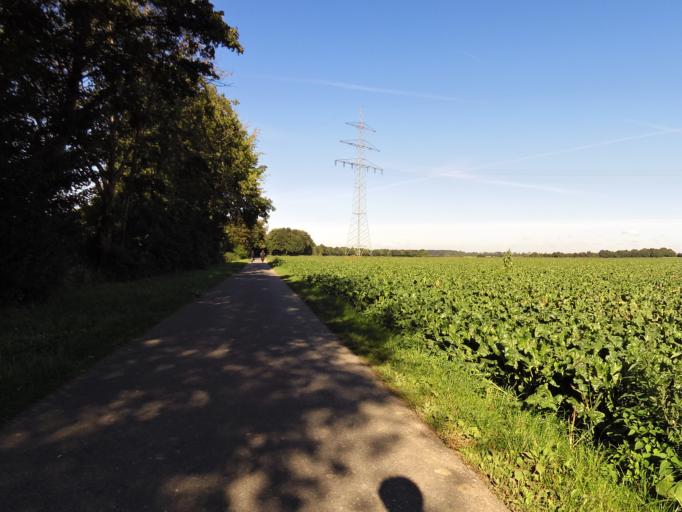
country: DE
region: North Rhine-Westphalia
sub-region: Regierungsbezirk Koln
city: Rheinbach
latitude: 50.6447
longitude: 6.9275
